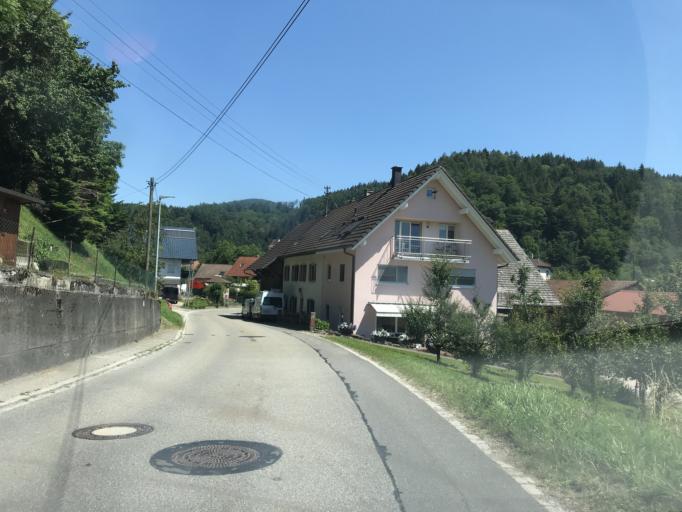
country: DE
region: Baden-Wuerttemberg
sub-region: Freiburg Region
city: Maulburg
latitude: 47.6875
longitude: 7.7958
